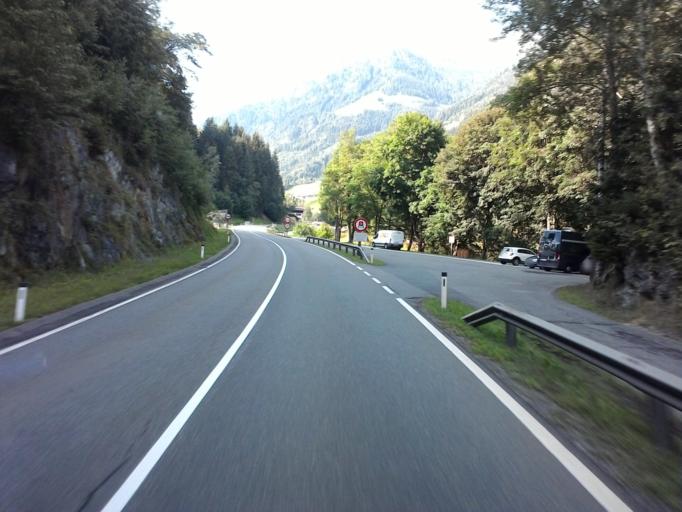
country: AT
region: Salzburg
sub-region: Politischer Bezirk Zell am See
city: Mittersill
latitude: 47.2702
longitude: 12.4861
